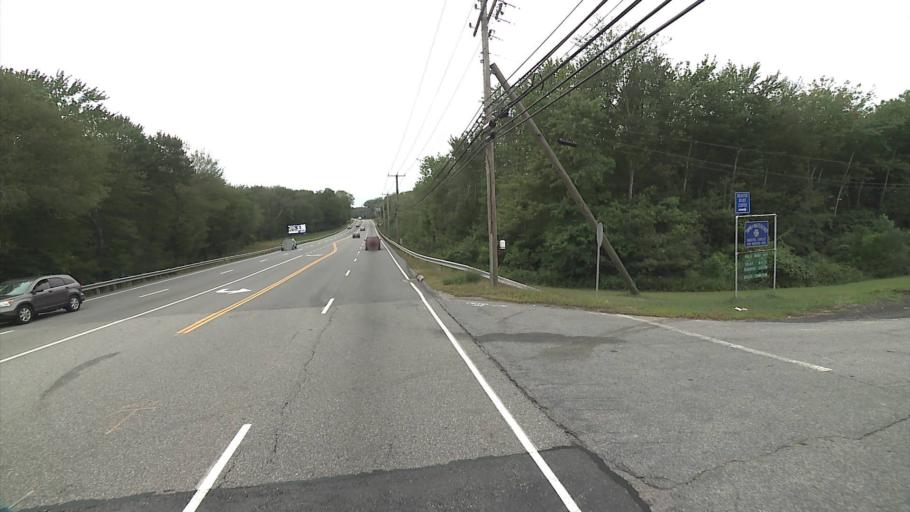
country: US
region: Connecticut
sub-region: New London County
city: Central Waterford
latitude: 41.3927
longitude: -72.1630
